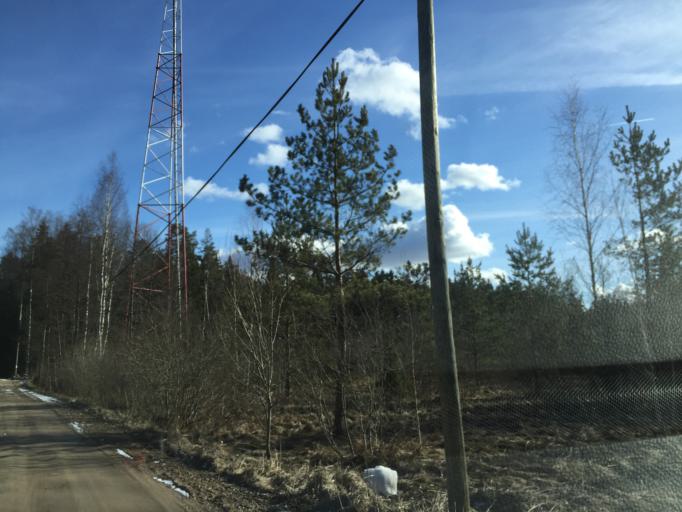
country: LV
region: Garkalne
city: Garkalne
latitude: 56.9537
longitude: 24.4407
